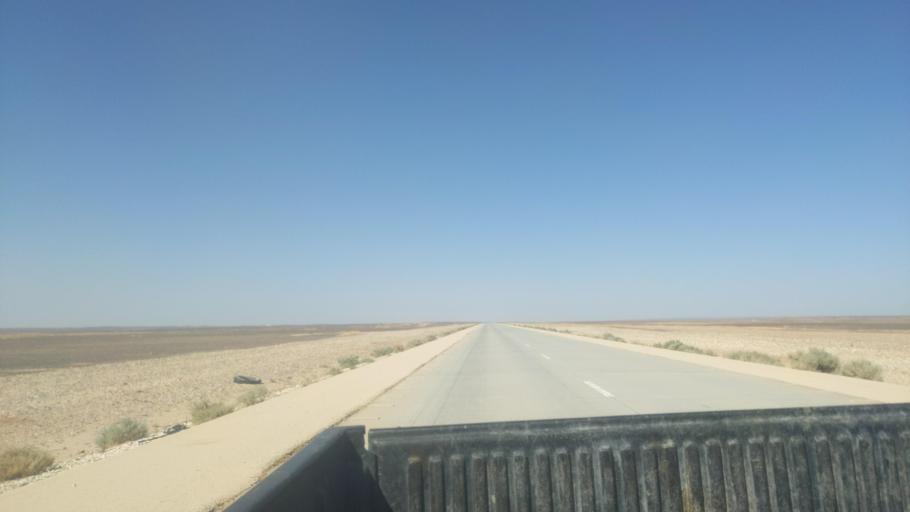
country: JO
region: Amman
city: Al Azraq ash Shamali
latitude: 31.4543
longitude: 36.7800
